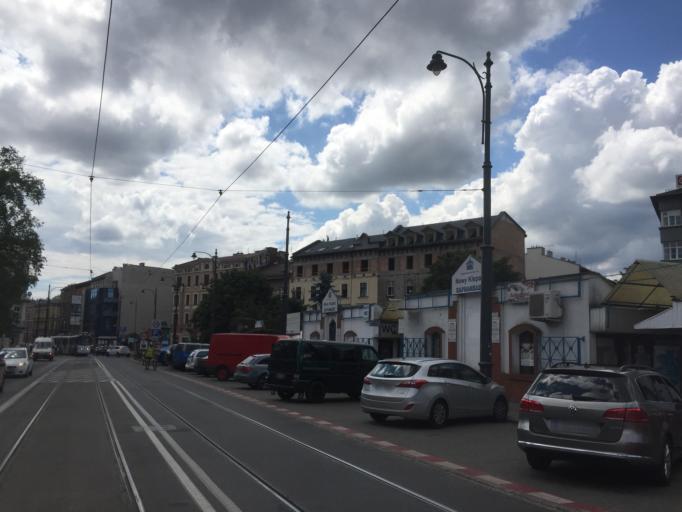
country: PL
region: Lesser Poland Voivodeship
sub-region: Krakow
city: Krakow
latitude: 50.0732
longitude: 19.9359
